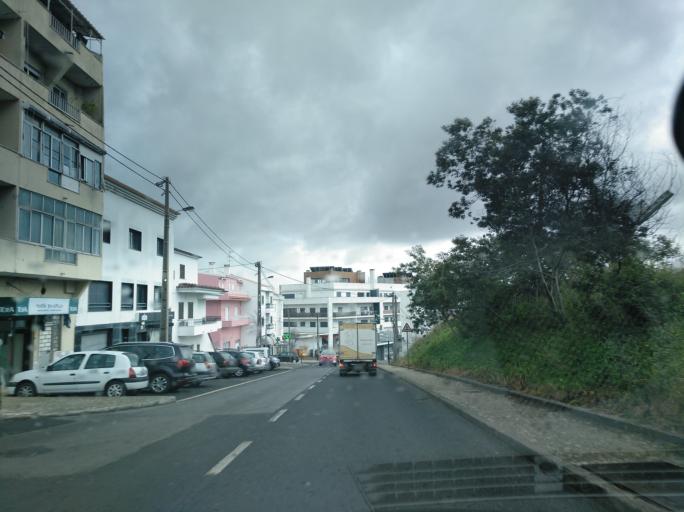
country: PT
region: Lisbon
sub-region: Odivelas
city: Famoes
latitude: 38.7846
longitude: -9.2075
